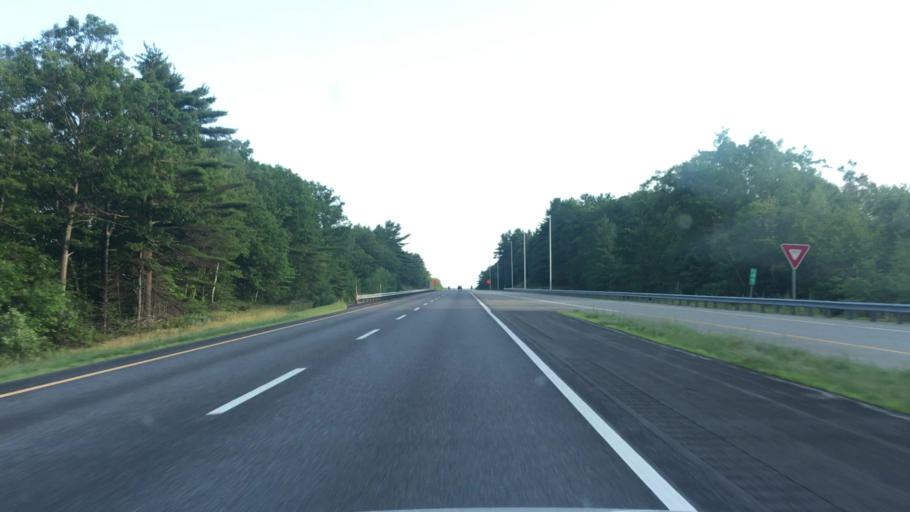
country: US
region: Maine
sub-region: Kennebec County
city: Gardiner
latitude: 44.1747
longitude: -69.8345
